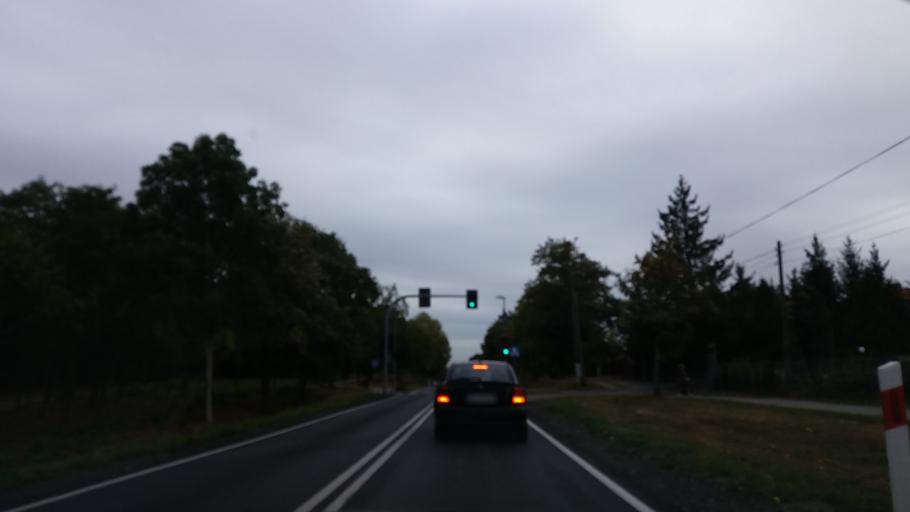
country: PL
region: Lubusz
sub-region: Powiat gorzowski
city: Klodawa
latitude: 52.7819
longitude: 15.2213
